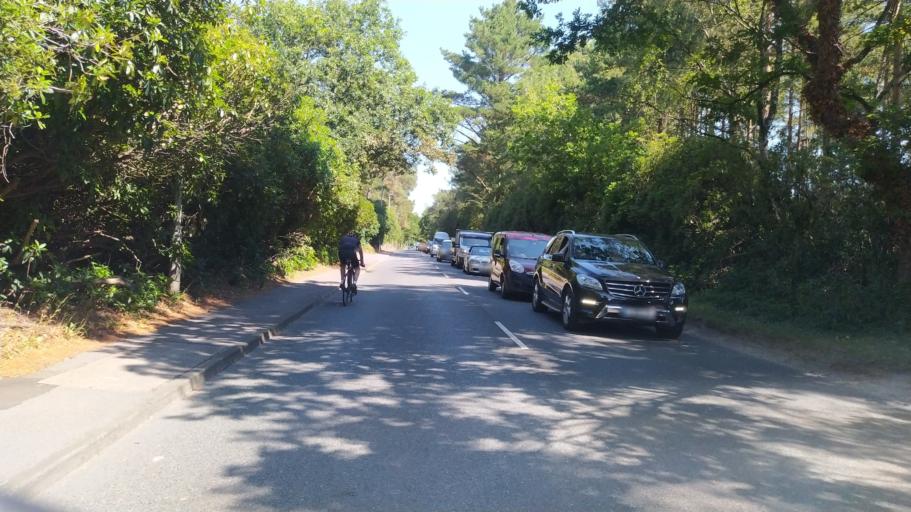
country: GB
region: England
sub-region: Dorset
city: Wareham
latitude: 50.7158
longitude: -2.0893
